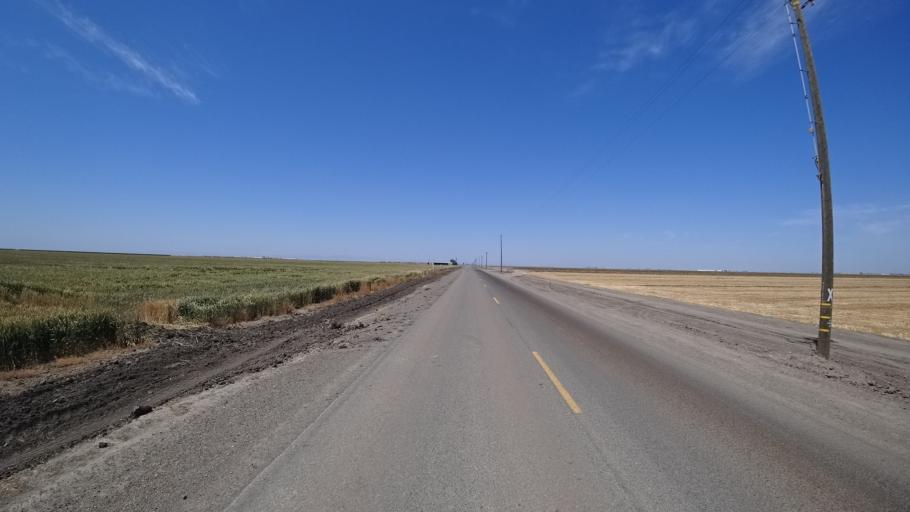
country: US
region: California
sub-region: Kings County
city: Corcoran
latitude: 36.1380
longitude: -119.6486
